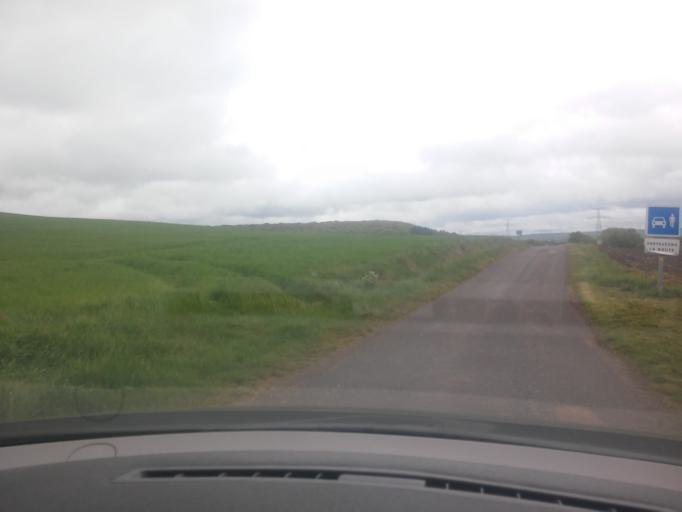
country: FR
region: Lorraine
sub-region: Departement de la Moselle
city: Courcelles-Chaussy
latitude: 49.1741
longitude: 6.4093
